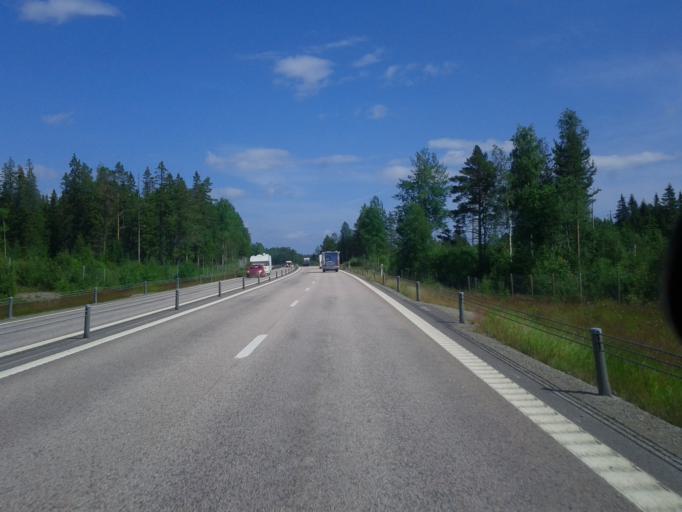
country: SE
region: Vaesterbotten
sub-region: Nordmalings Kommun
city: Nordmaling
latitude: 63.5016
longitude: 19.3382
